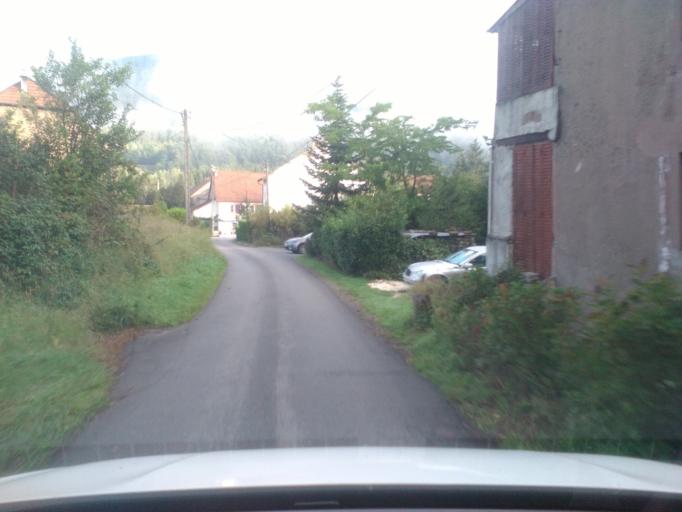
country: FR
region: Lorraine
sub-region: Departement des Vosges
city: Moyenmoutier
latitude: 48.3895
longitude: 6.9007
